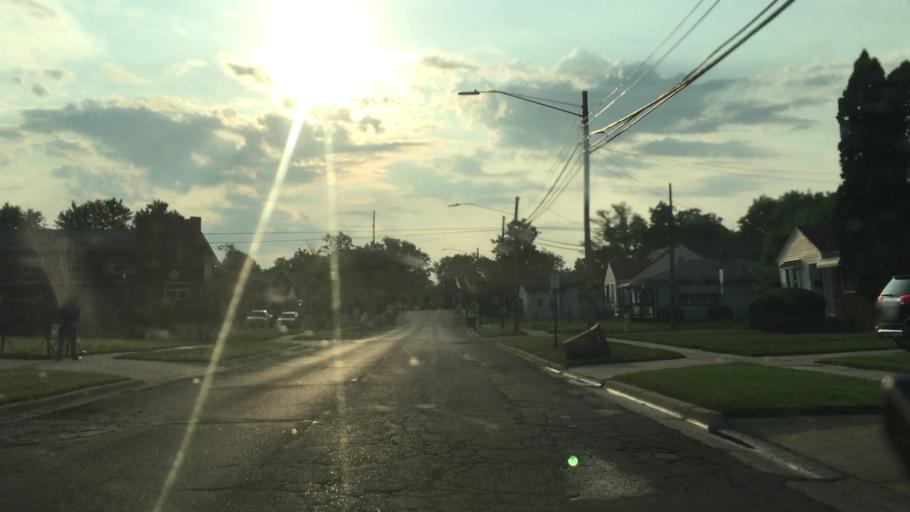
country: US
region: Michigan
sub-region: Oakland County
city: Pontiac
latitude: 42.6381
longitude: -83.2716
